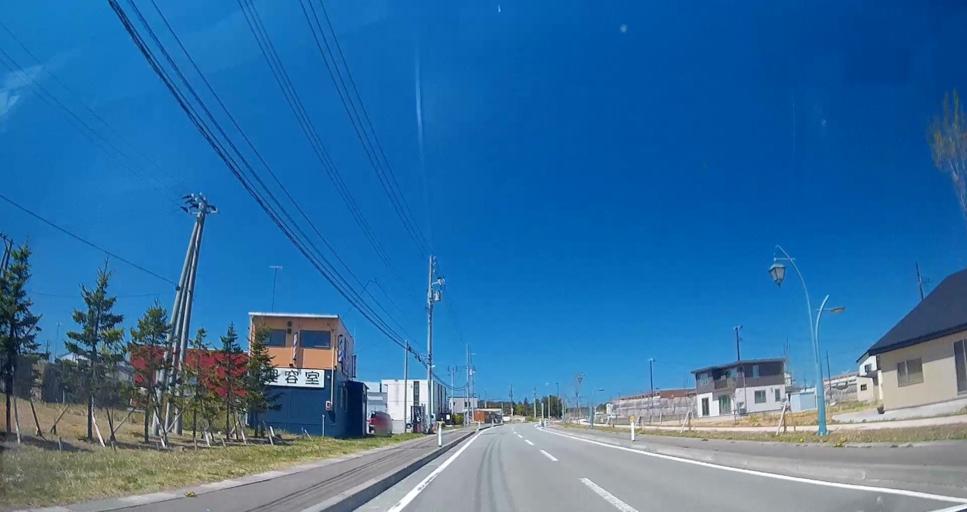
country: JP
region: Aomori
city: Misawa
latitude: 40.9691
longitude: 141.3636
